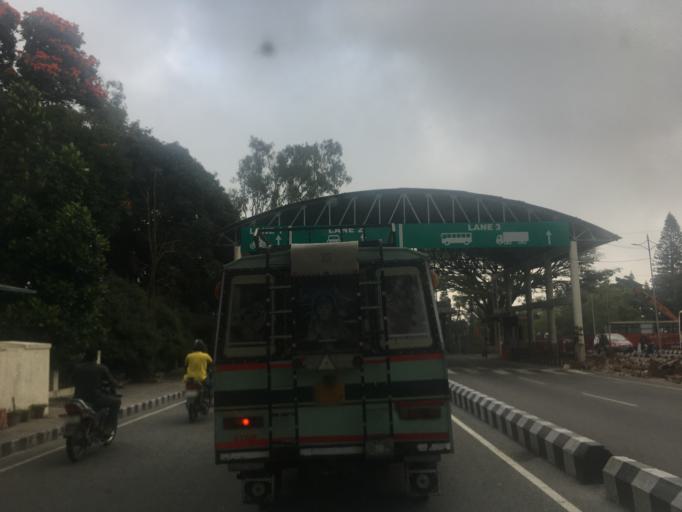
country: IN
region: Andhra Pradesh
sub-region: Chittoor
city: Tirumala
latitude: 13.6726
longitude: 79.3513
